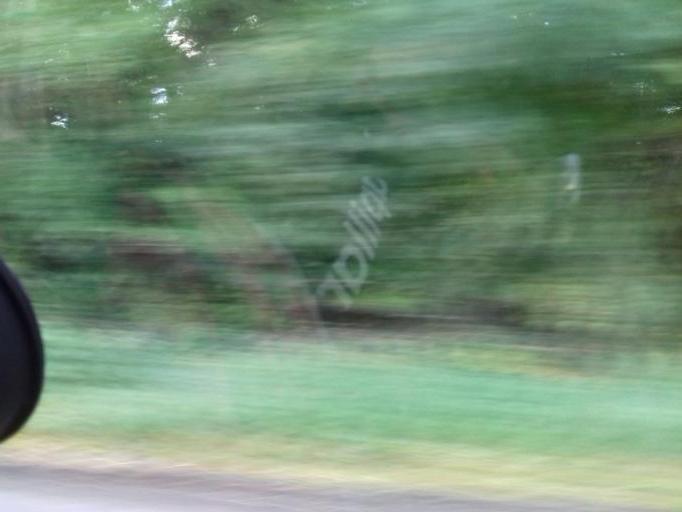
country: IE
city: Kentstown
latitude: 53.6328
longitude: -6.4934
